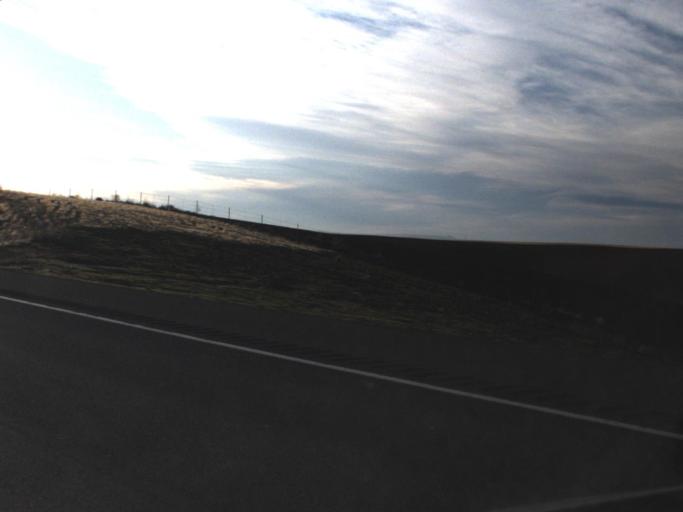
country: US
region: Washington
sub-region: Walla Walla County
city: Garrett
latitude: 46.0679
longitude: -118.4225
